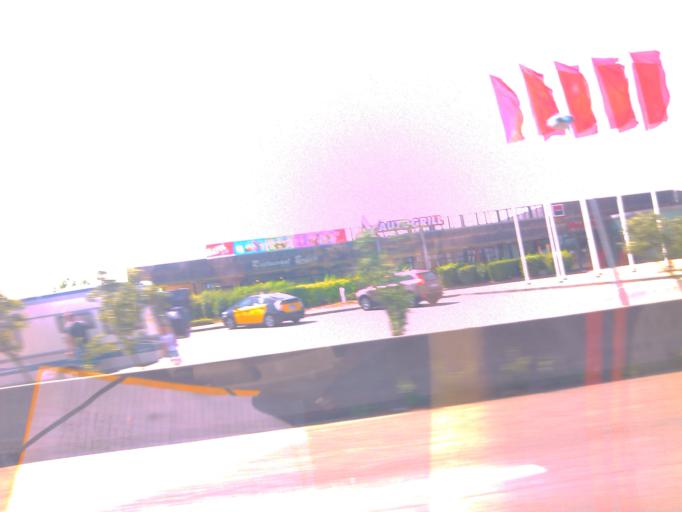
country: FR
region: Rhone-Alpes
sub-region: Departement de l'Ain
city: Guereins
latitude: 46.1423
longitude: 4.7682
